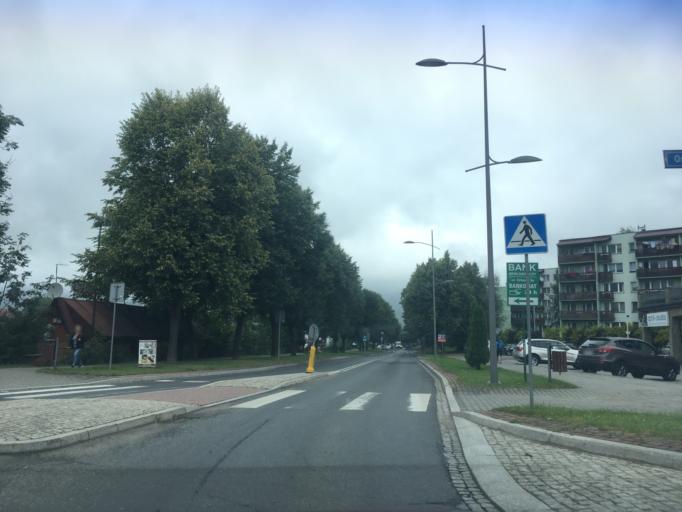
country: PL
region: Lesser Poland Voivodeship
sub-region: Powiat nowotarski
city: Rabka-Zdroj
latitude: 49.6100
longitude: 19.9530
